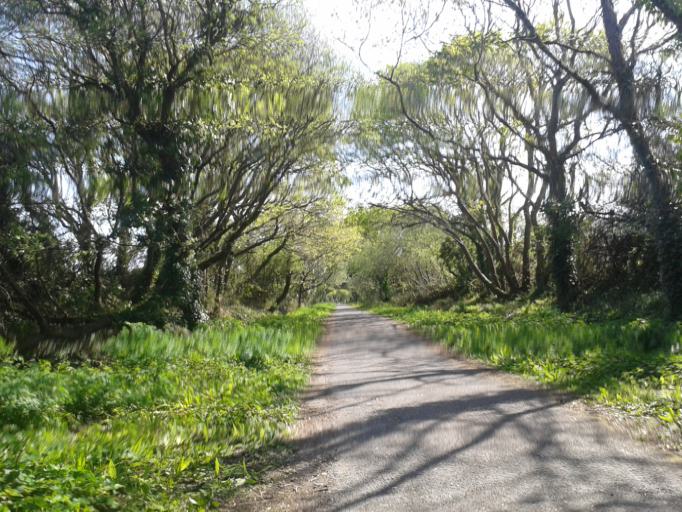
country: GB
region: England
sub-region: Devon
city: Braunton
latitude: 51.0935
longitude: -4.1336
